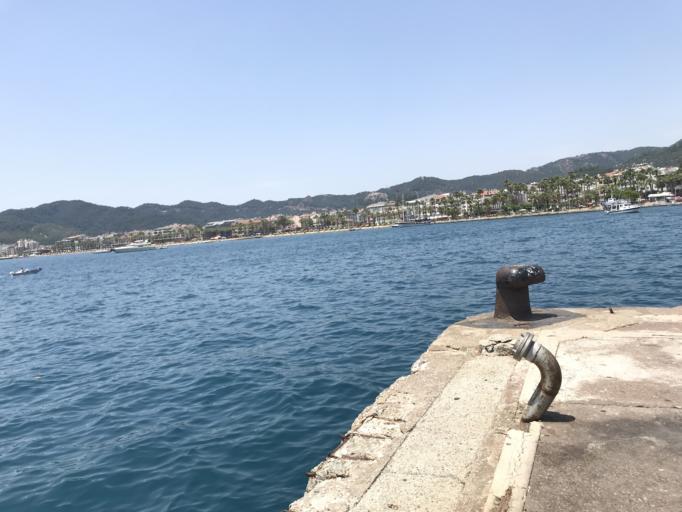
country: TR
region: Mugla
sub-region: Marmaris
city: Marmaris
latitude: 36.8512
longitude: 28.2728
